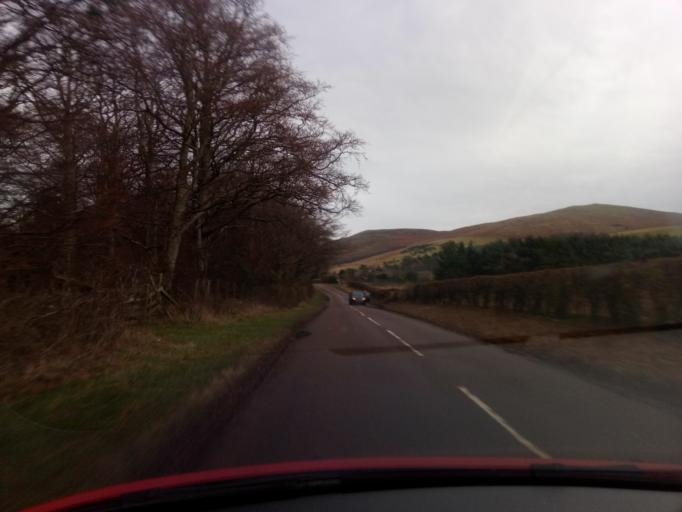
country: GB
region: England
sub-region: Northumberland
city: Kirknewton
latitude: 55.5669
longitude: -2.1049
